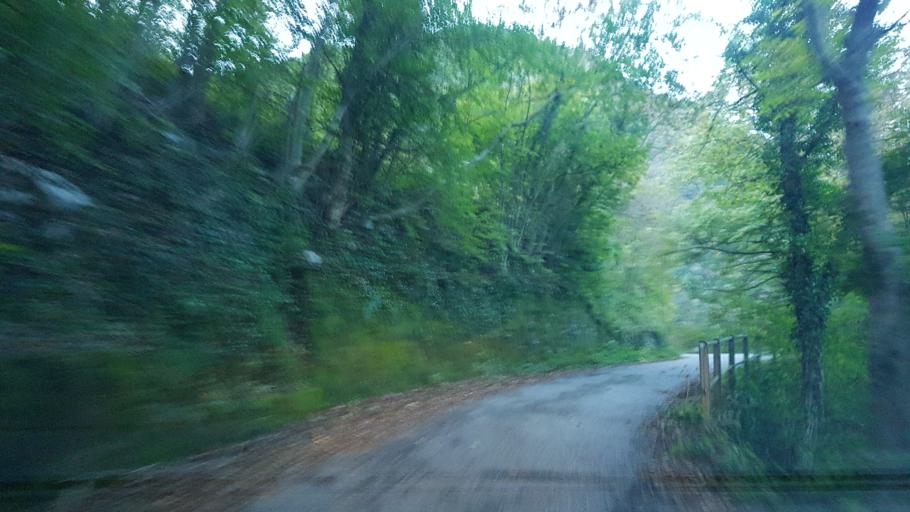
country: IT
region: Friuli Venezia Giulia
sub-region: Provincia di Udine
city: Venzone
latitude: 46.3338
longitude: 13.1514
